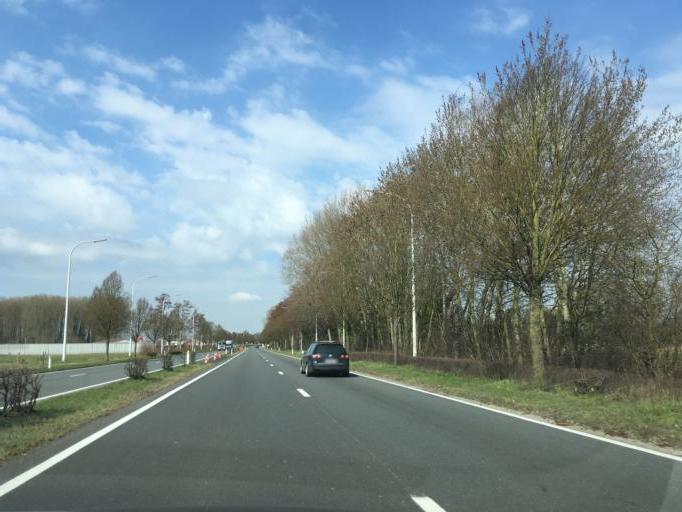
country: BE
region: Flanders
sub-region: Provincie West-Vlaanderen
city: Deerlijk
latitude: 50.8464
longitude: 3.3475
